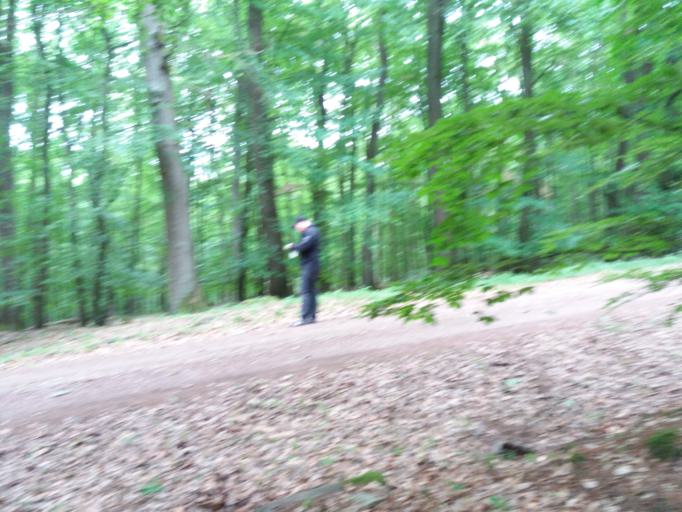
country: DE
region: Hesse
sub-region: Regierungsbezirk Darmstadt
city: Niedernhausen
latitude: 50.1565
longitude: 8.2868
